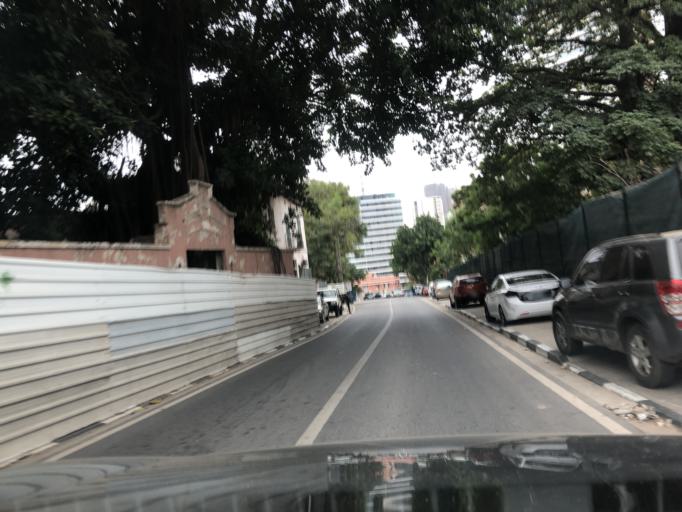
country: AO
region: Luanda
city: Luanda
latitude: -8.8166
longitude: 13.2272
